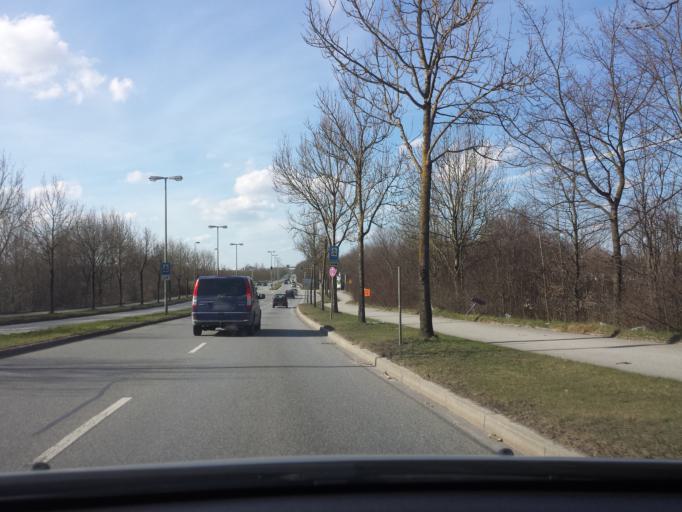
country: DE
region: Bavaria
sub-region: Upper Bavaria
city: Karlsfeld
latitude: 48.2003
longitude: 11.4927
